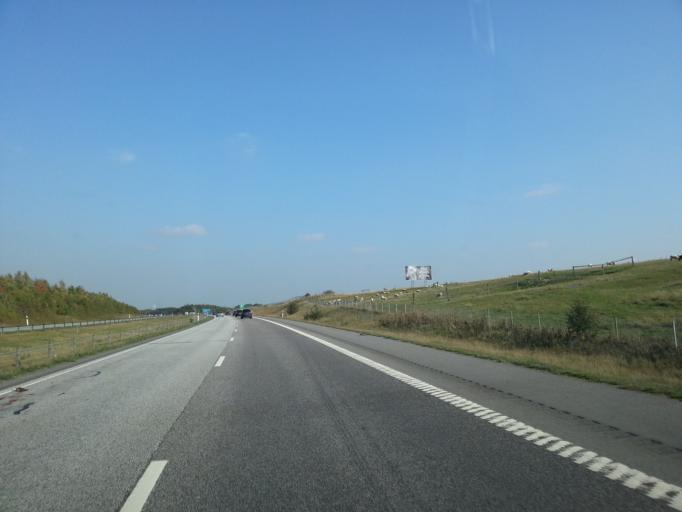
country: SE
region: Skane
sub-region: Malmo
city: Oxie
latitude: 55.5723
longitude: 13.1012
